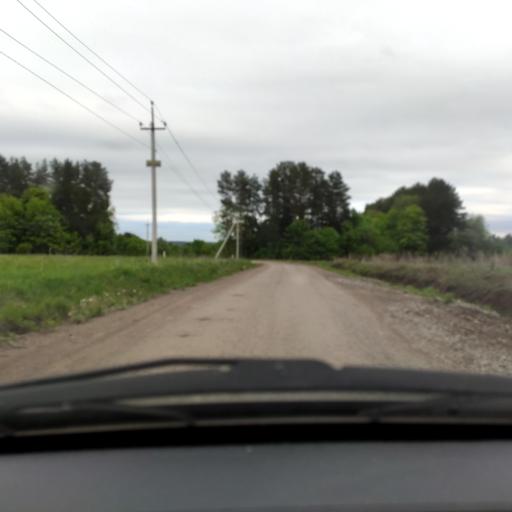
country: RU
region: Bashkortostan
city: Kabakovo
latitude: 54.6209
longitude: 56.1614
